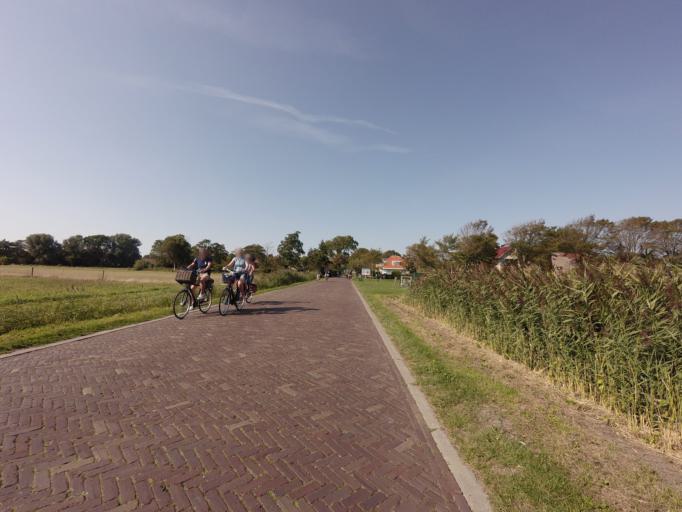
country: NL
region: Friesland
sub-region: Gemeente Schiermonnikoog
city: Schiermonnikoog
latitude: 53.4759
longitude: 6.1617
